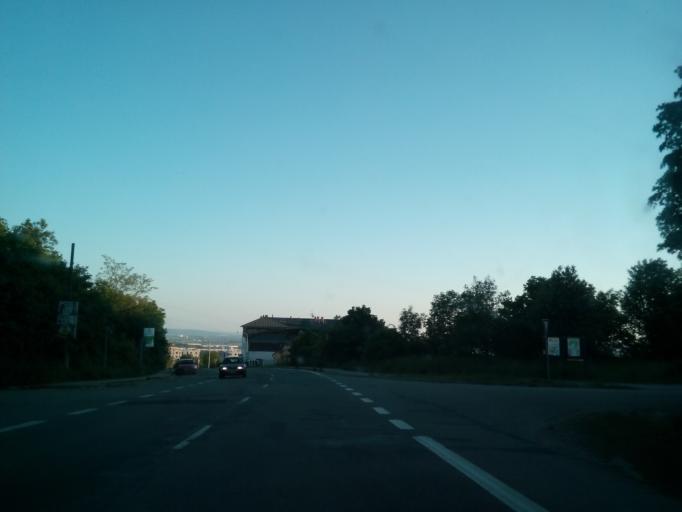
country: CZ
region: South Moravian
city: Bilovice nad Svitavou
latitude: 49.2184
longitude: 16.6815
